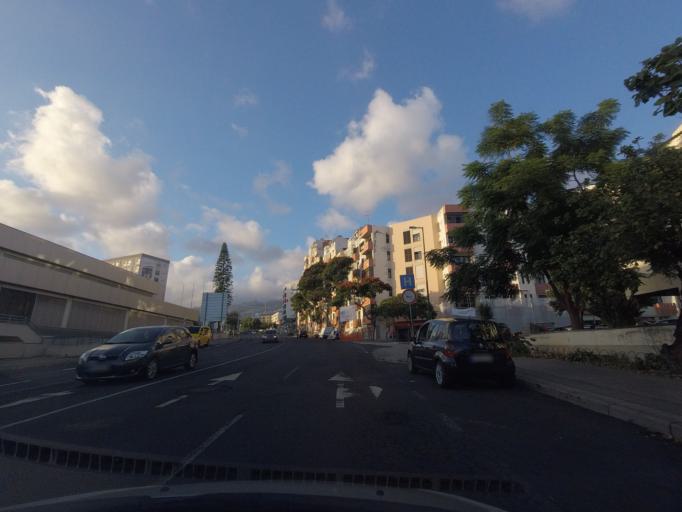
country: PT
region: Madeira
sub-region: Funchal
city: Funchal
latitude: 32.6475
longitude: -16.9229
